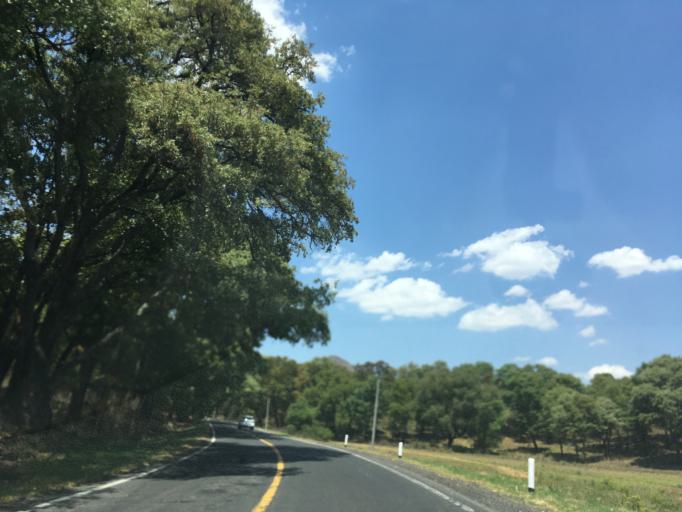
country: MX
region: Michoacan
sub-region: Chilchota
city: Tacuro (Santa Maria Tacuro)
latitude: 19.8080
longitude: -102.0254
